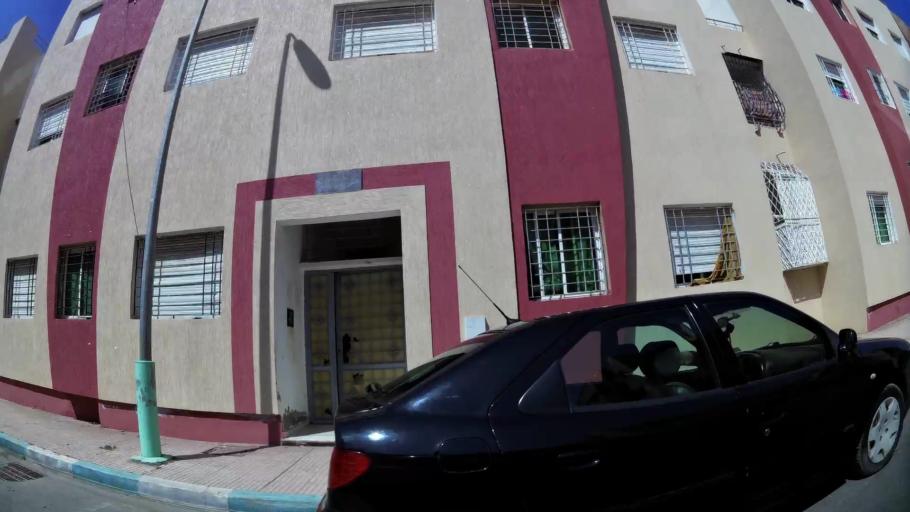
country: MA
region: Rabat-Sale-Zemmour-Zaer
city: Sale
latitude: 34.0713
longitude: -6.7558
